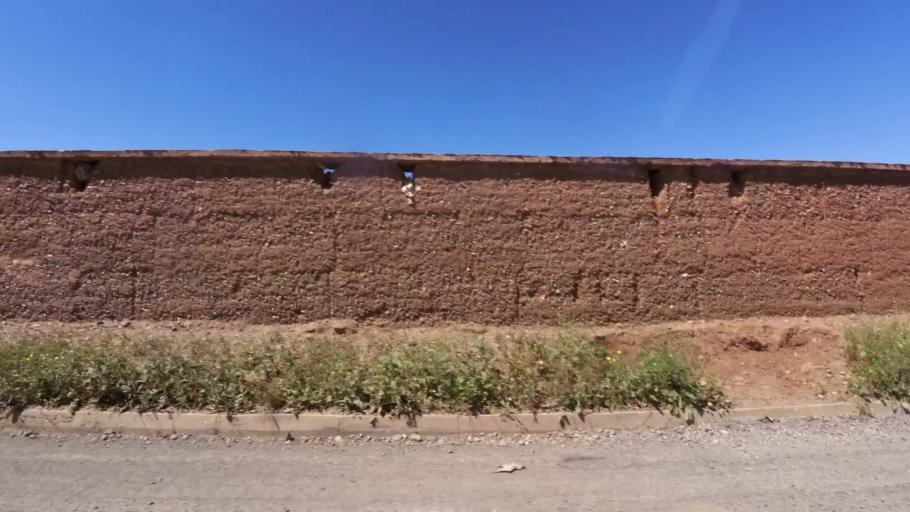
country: MA
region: Marrakech-Tensift-Al Haouz
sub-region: Marrakech
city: Marrakesh
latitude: 31.5854
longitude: -8.0055
